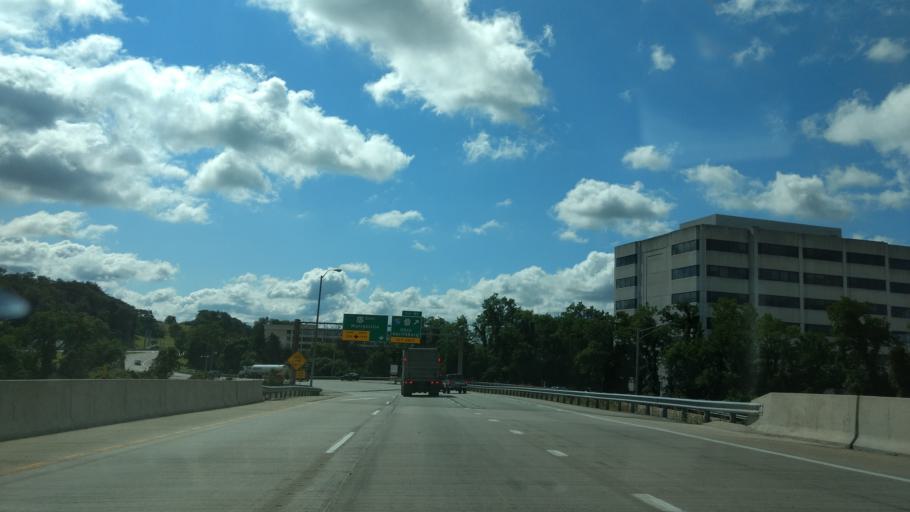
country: US
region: Pennsylvania
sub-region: Allegheny County
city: Monroeville
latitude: 40.4388
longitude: -79.7587
